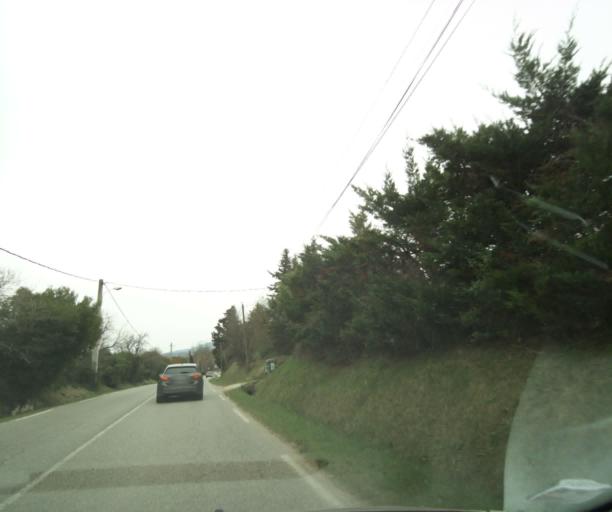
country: FR
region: Provence-Alpes-Cote d'Azur
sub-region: Departement des Bouches-du-Rhone
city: Trets
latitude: 43.4499
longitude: 5.6714
